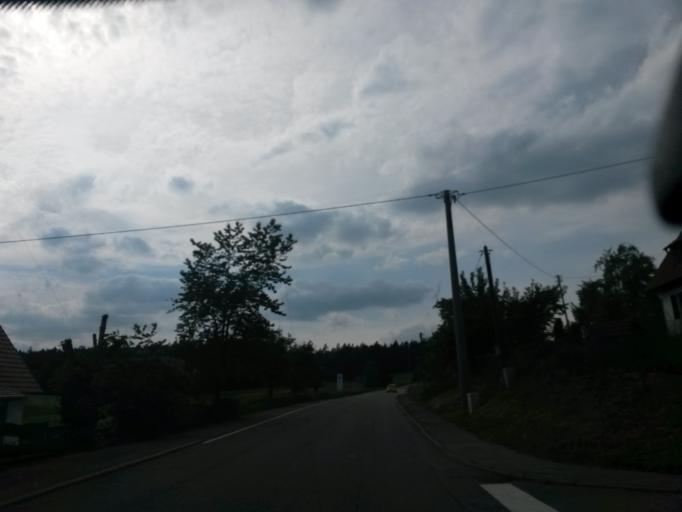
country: DE
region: Baden-Wuerttemberg
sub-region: Karlsruhe Region
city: Oberreichenbach
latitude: 48.7346
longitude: 8.6606
